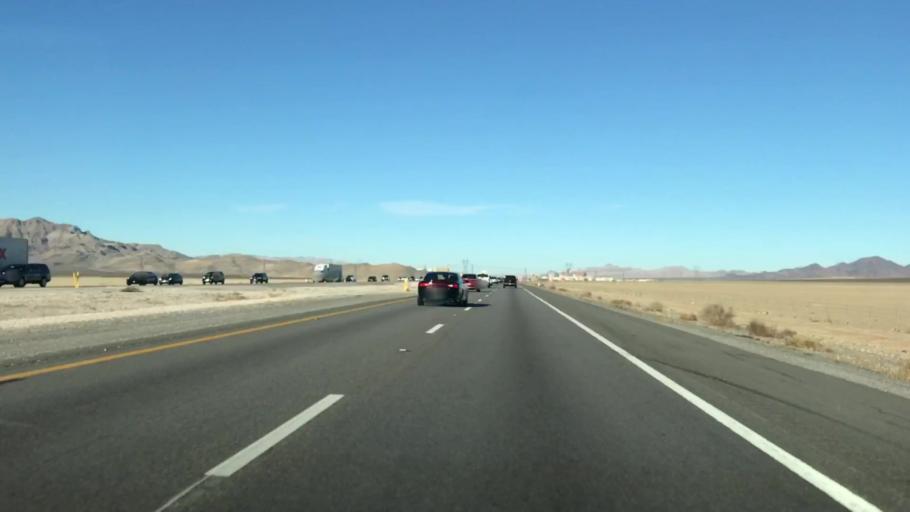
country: US
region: Nevada
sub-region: Clark County
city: Sandy Valley
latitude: 35.5776
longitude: -115.4032
